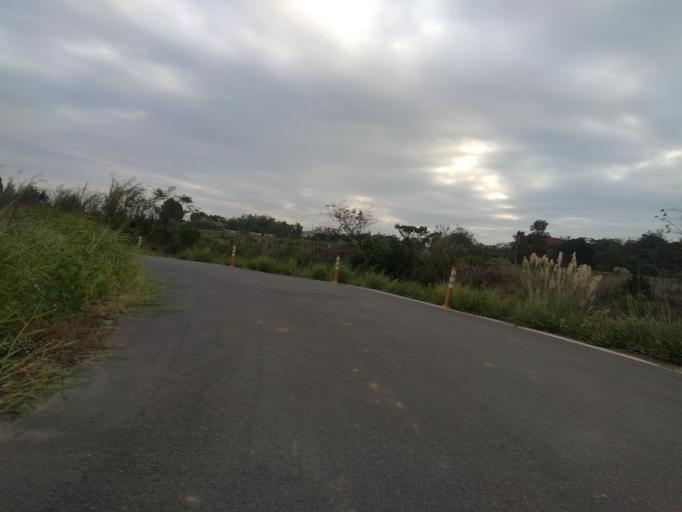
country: TW
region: Taiwan
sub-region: Hsinchu
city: Zhubei
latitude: 24.9775
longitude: 121.0294
